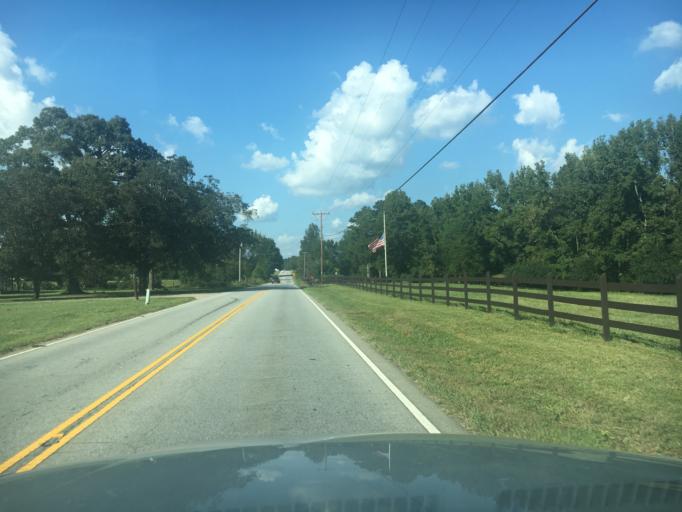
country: US
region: South Carolina
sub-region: Greenville County
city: Fountain Inn
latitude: 34.6680
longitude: -82.2606
